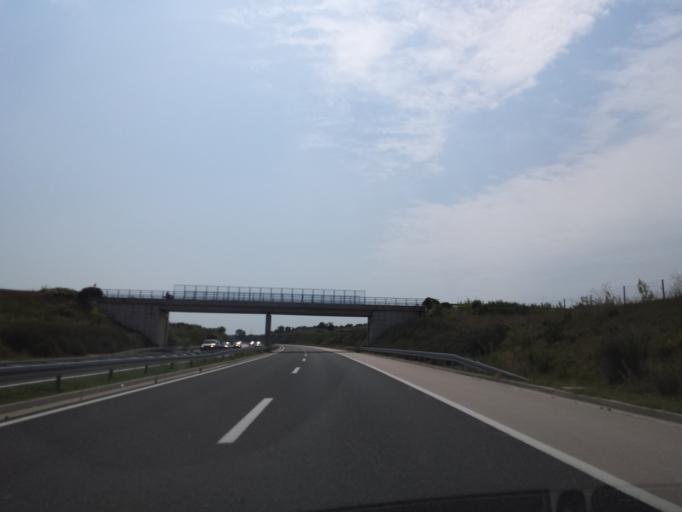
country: HR
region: Zadarska
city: Policnik
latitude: 44.1630
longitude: 15.4192
